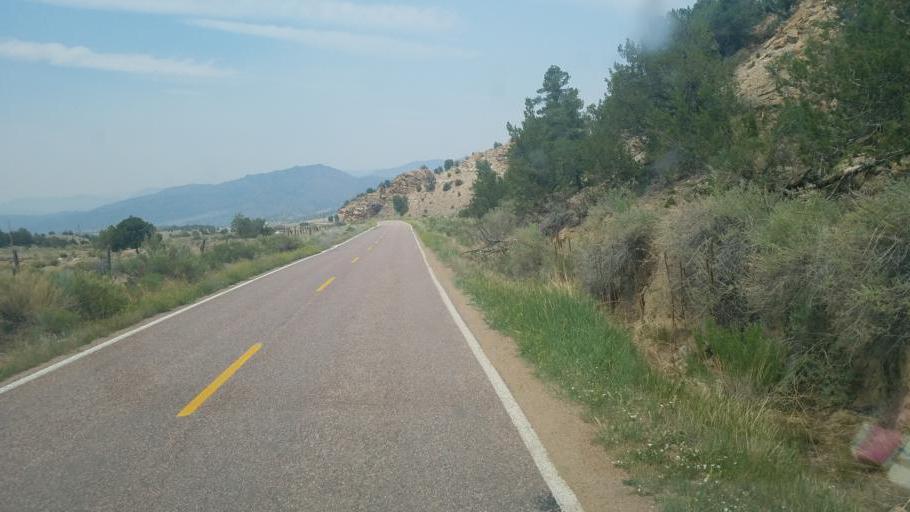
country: US
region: Colorado
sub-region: Fremont County
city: Canon City
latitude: 38.4460
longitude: -105.3735
